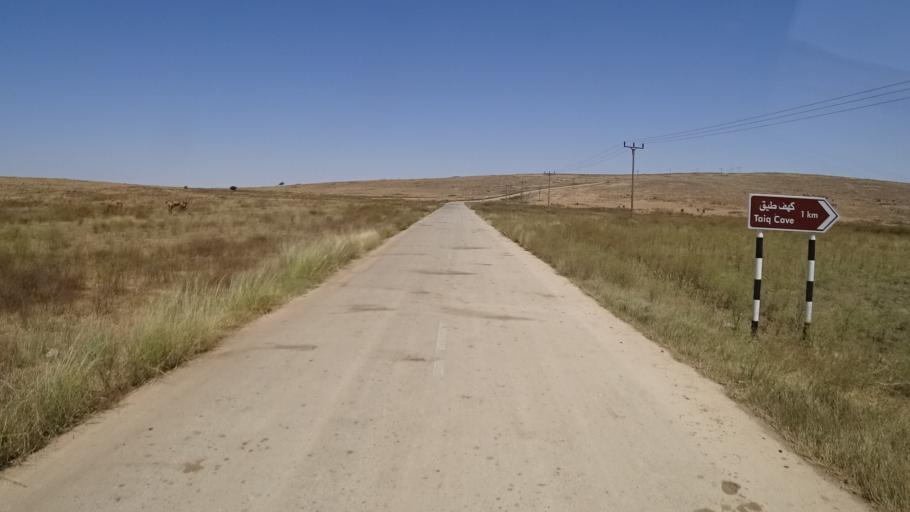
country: OM
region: Zufar
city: Salalah
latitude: 17.1540
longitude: 54.6182
